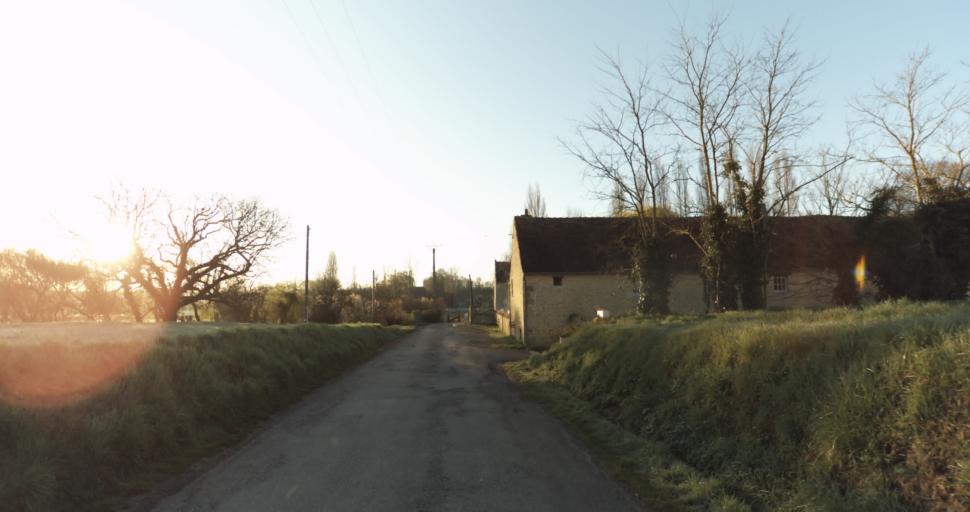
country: FR
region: Lower Normandy
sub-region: Departement du Calvados
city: Saint-Pierre-sur-Dives
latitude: 49.0310
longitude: -0.0275
